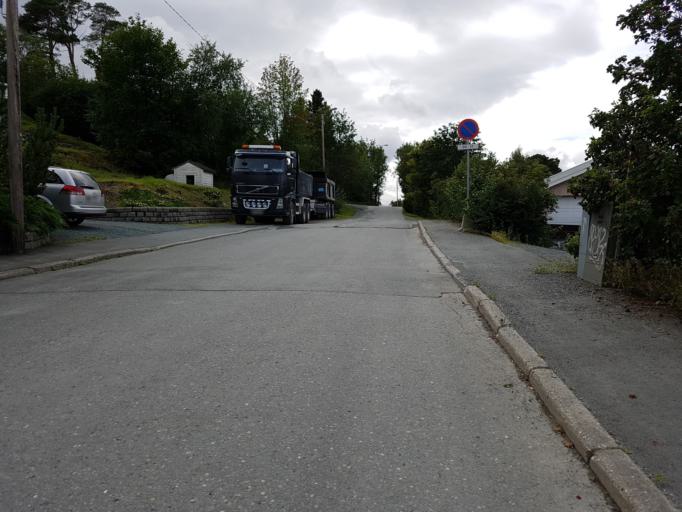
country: NO
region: Sor-Trondelag
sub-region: Trondheim
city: Trondheim
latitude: 63.4184
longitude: 10.4727
